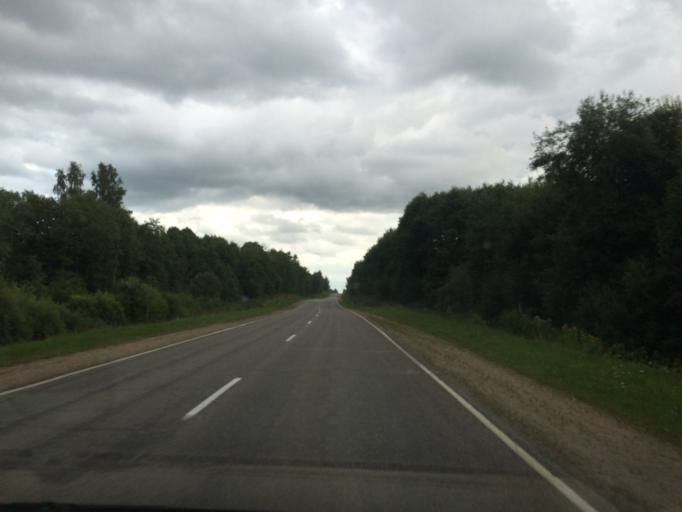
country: LV
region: Rezekne
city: Rezekne
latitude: 56.5540
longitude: 27.3599
